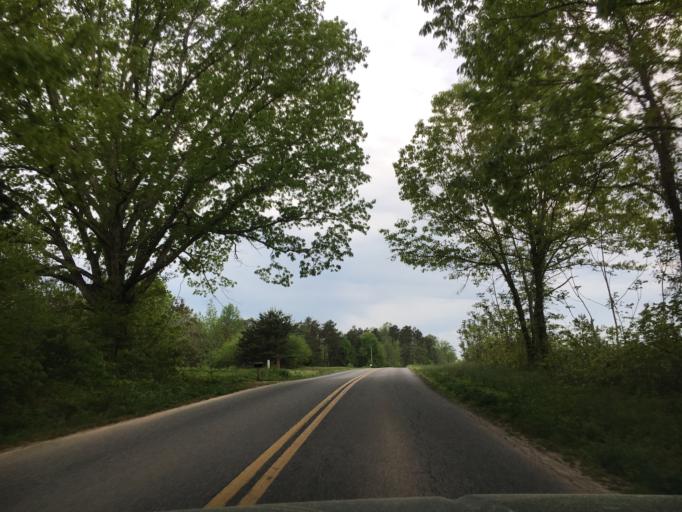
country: US
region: Virginia
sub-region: Halifax County
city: Halifax
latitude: 36.9079
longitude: -78.9329
